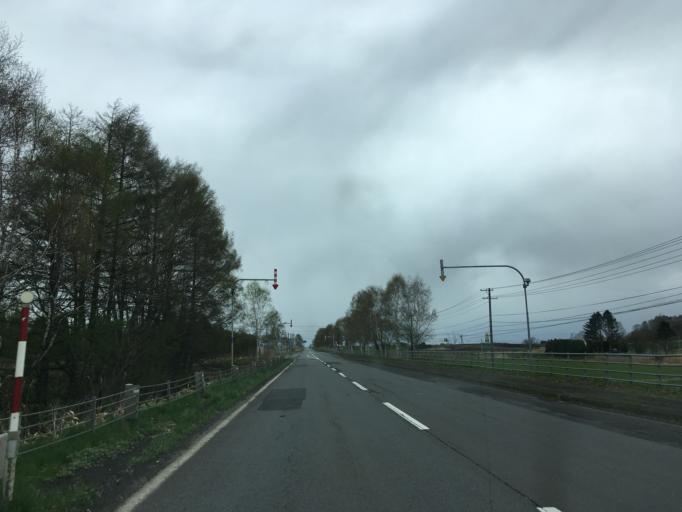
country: JP
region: Hokkaido
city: Chitose
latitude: 42.9134
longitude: 141.8107
